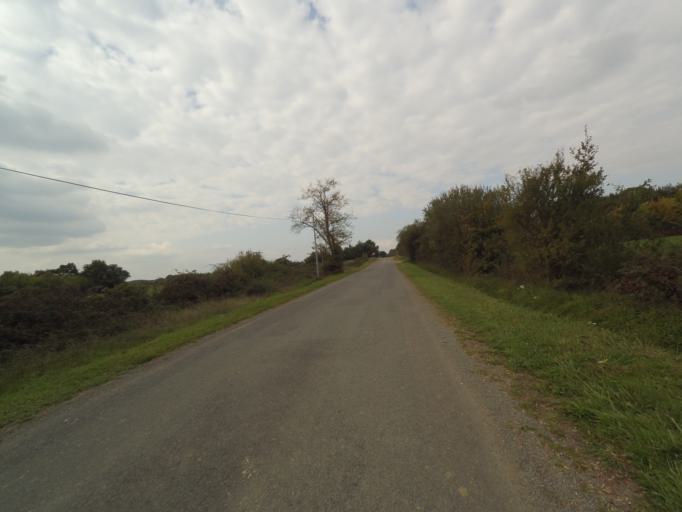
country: FR
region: Pays de la Loire
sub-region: Departement de la Vendee
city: Bouffere
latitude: 46.9832
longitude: -1.3525
